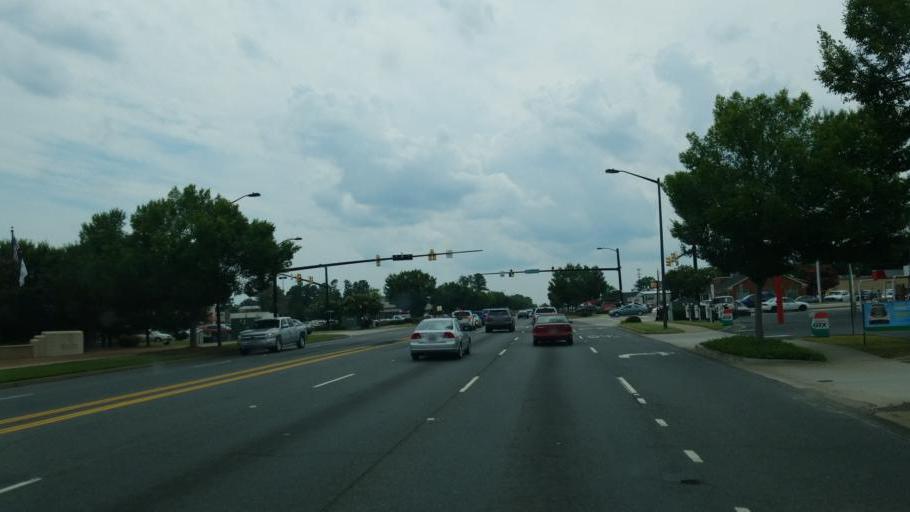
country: US
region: South Carolina
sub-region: York County
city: Rock Hill
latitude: 34.9637
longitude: -81.0009
